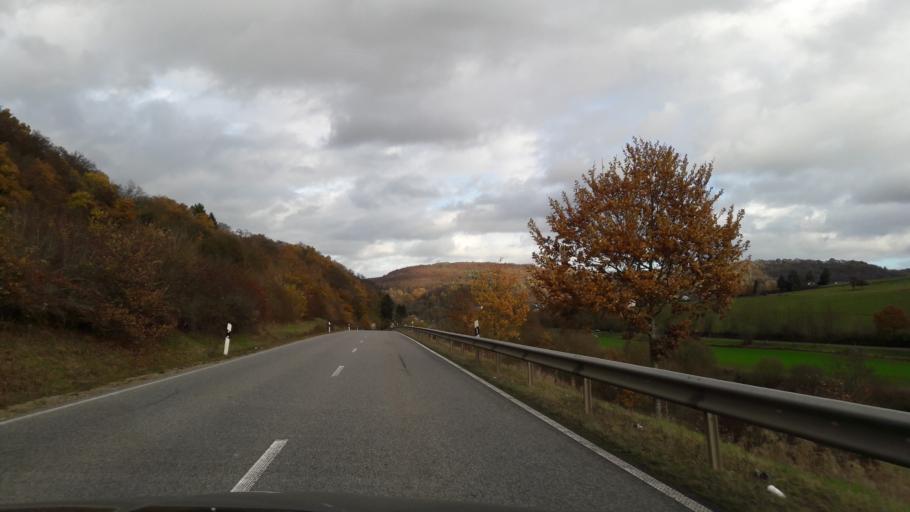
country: DE
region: Rheinland-Pfalz
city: Minden
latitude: 49.8166
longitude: 6.4589
